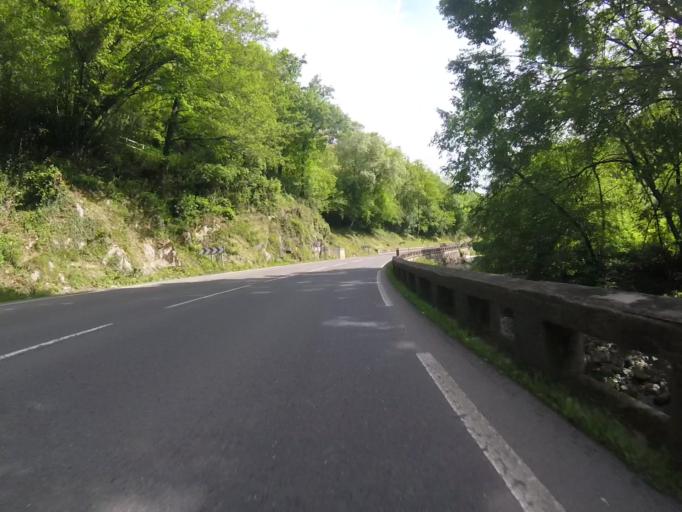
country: ES
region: Basque Country
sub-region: Provincia de Guipuzcoa
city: Azkoitia
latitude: 43.1598
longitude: -2.3348
